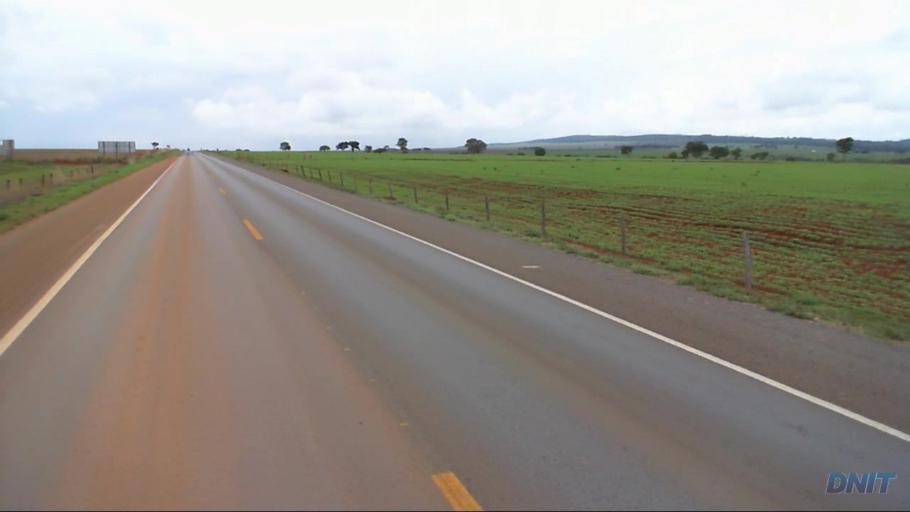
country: BR
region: Goias
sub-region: Padre Bernardo
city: Padre Bernardo
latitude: -15.1652
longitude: -48.3627
